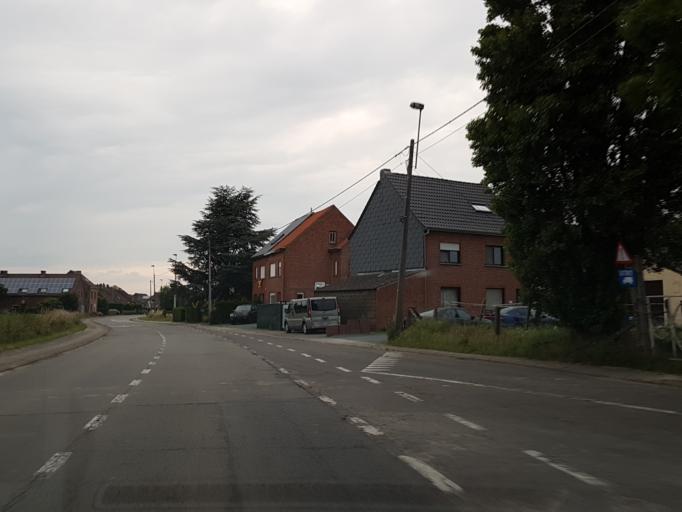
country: BE
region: Flanders
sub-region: Provincie Vlaams-Brabant
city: Kapelle-op-den-Bos
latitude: 50.9977
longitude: 4.3648
